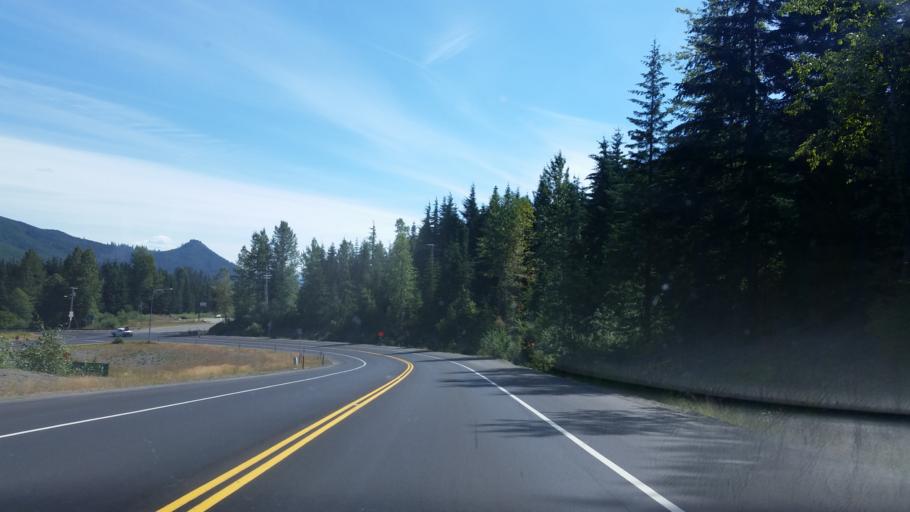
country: US
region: Washington
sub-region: King County
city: Tanner
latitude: 47.3966
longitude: -121.3998
